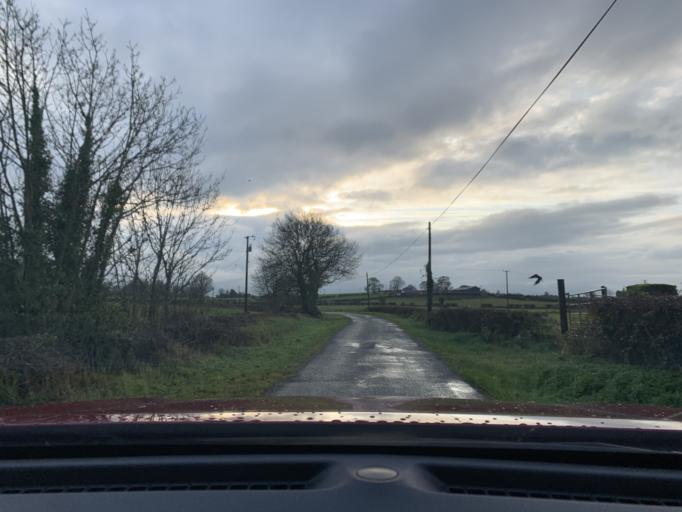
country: IE
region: Connaught
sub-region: Sligo
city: Ballymote
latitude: 54.0384
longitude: -8.5488
